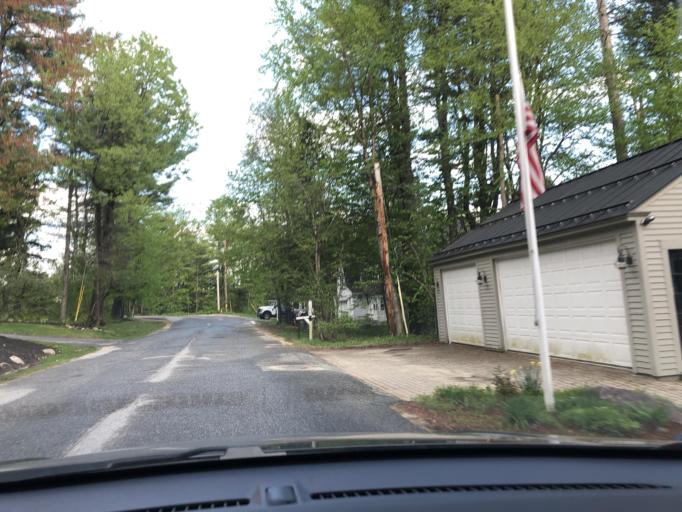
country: US
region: New Hampshire
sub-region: Merrimack County
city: New London
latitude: 43.4097
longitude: -71.9791
